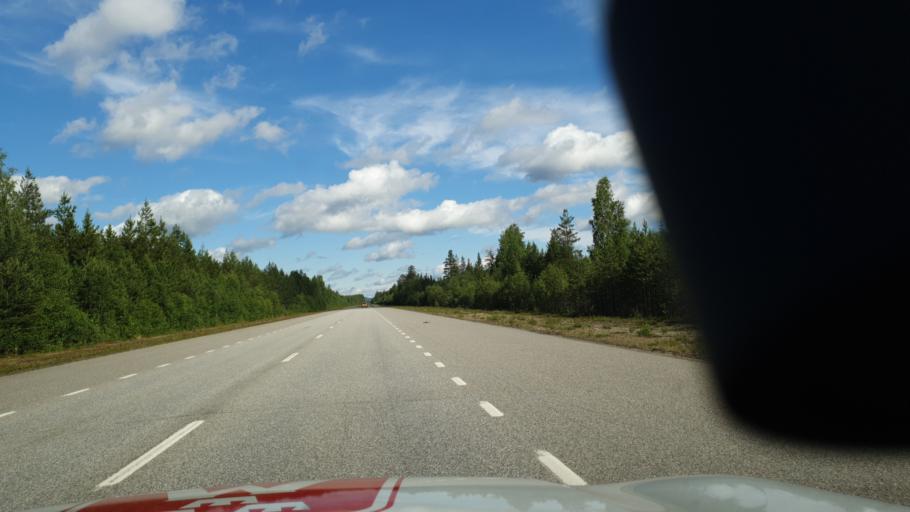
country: SE
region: Vaesterbotten
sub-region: Norsjo Kommun
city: Norsjoe
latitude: 64.5675
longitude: 19.3131
